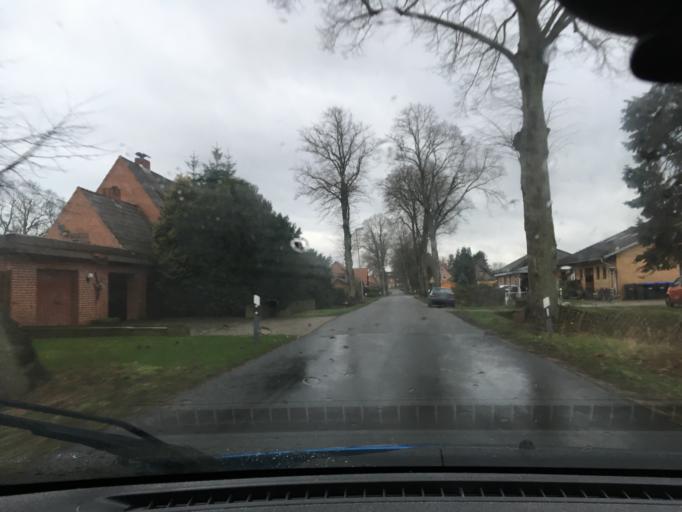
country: DE
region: Lower Saxony
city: Hittbergen
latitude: 53.3475
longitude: 10.5953
